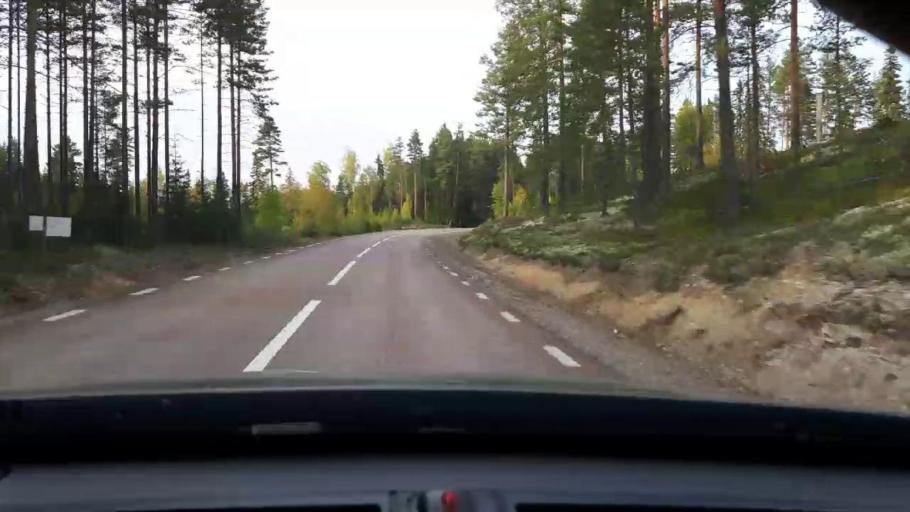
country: SE
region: Dalarna
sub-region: Gagnefs Kommun
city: Mockfjard
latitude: 60.3304
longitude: 14.9237
